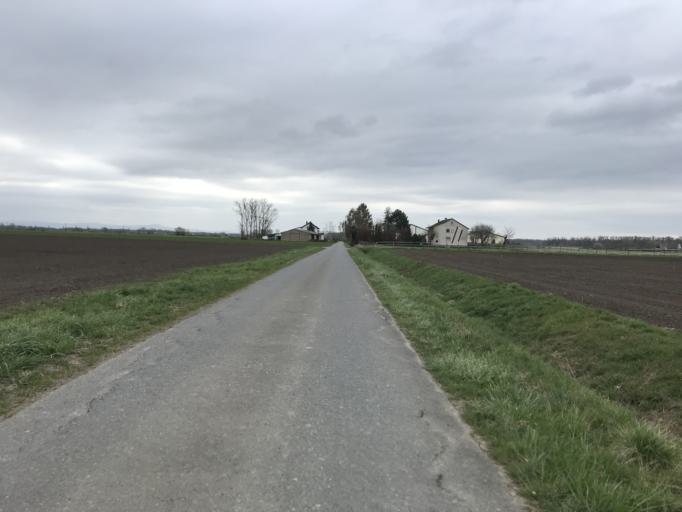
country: DE
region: Rheinland-Pfalz
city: Oppenheim
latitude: 49.8711
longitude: 8.3769
